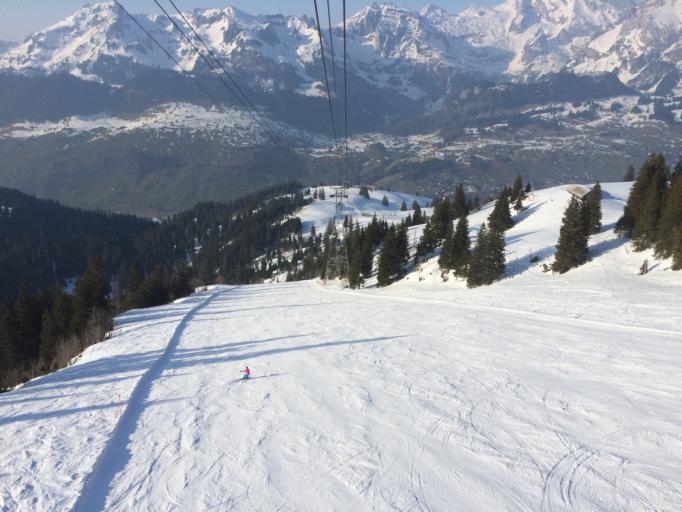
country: CH
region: Saint Gallen
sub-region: Wahlkreis Sarganserland
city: Walenstadt
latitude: 47.1728
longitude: 9.3120
